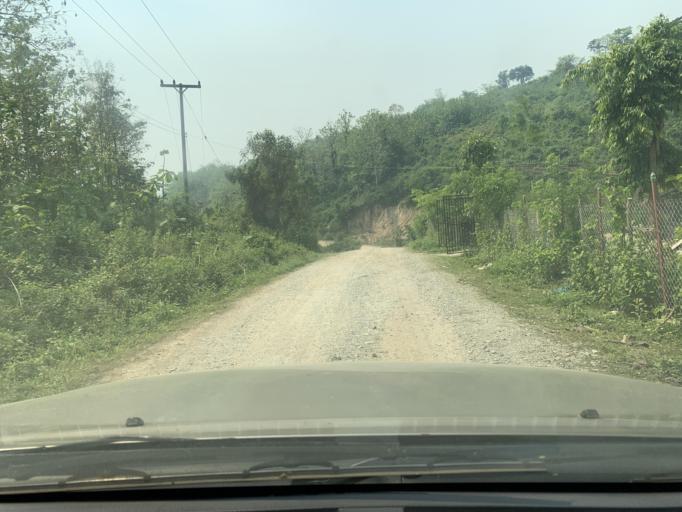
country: LA
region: Louangphabang
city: Louangphabang
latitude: 19.8826
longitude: 102.2583
